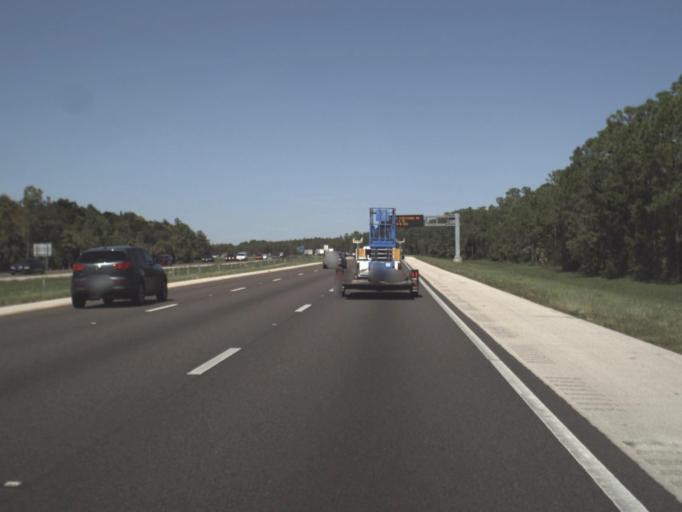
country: US
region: Florida
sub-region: Lee County
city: Bonita Springs
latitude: 26.3038
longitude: -81.7428
